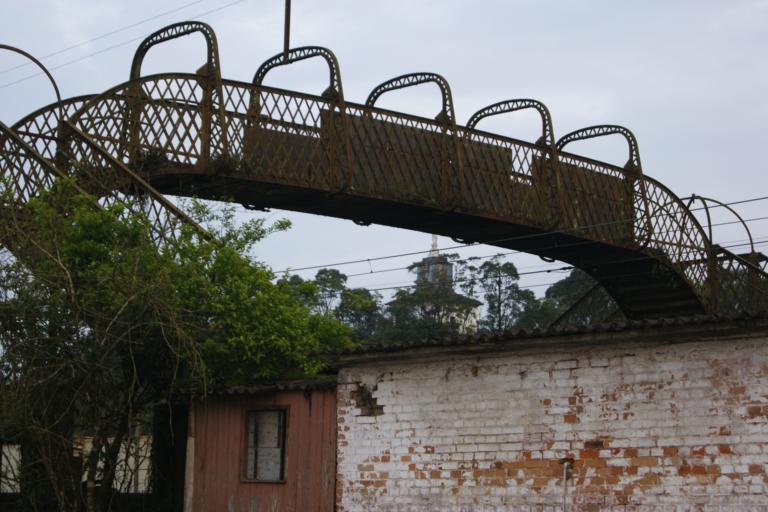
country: BR
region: Sao Paulo
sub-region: Rio Grande Da Serra
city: Rio Grande da Serra
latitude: -23.7678
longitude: -46.3424
